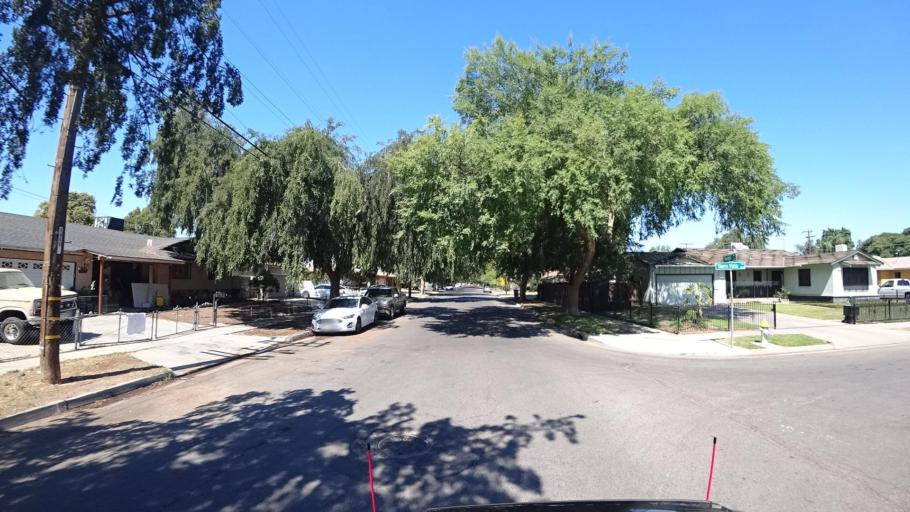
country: US
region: California
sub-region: Fresno County
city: Fresno
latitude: 36.7218
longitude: -119.7407
